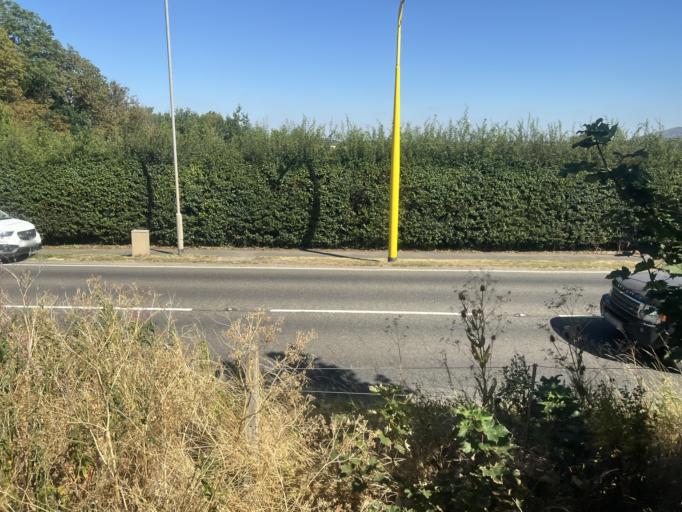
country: GB
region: England
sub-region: Lincolnshire
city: Kirton
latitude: 52.9753
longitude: -0.1088
